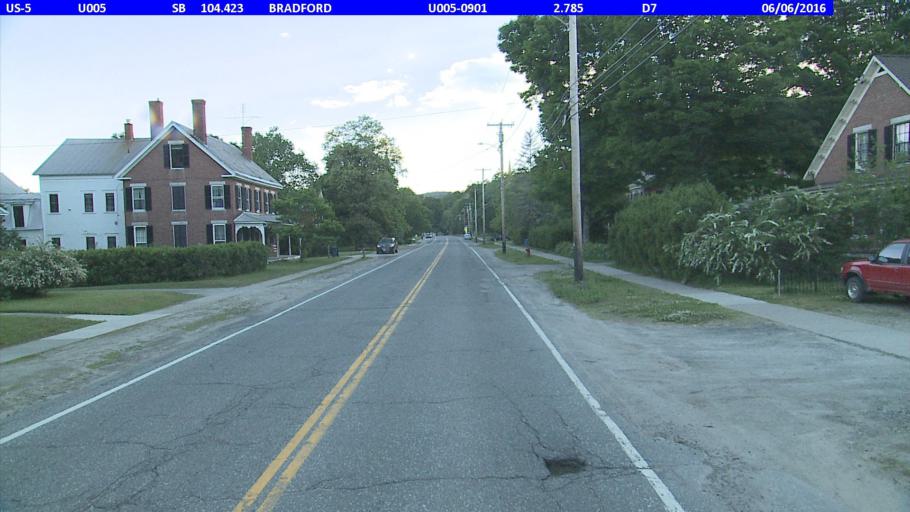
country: US
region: New Hampshire
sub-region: Grafton County
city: Haverhill
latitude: 43.9992
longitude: -72.1249
